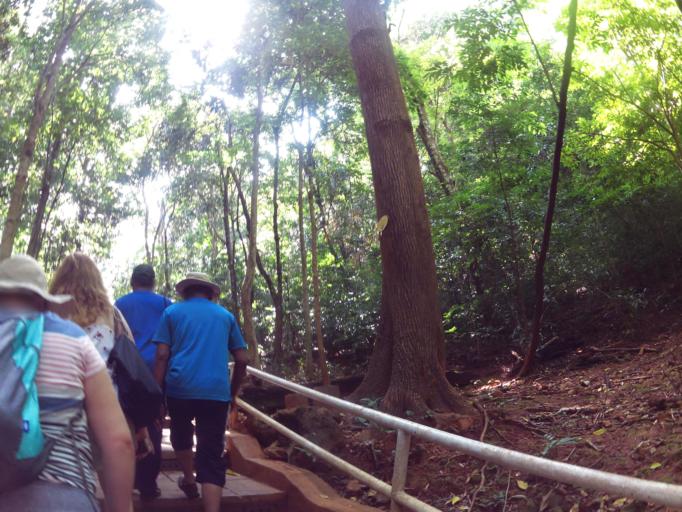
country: MY
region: Kedah
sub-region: Langkawi
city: Kuah
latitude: 6.2084
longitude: 99.7835
